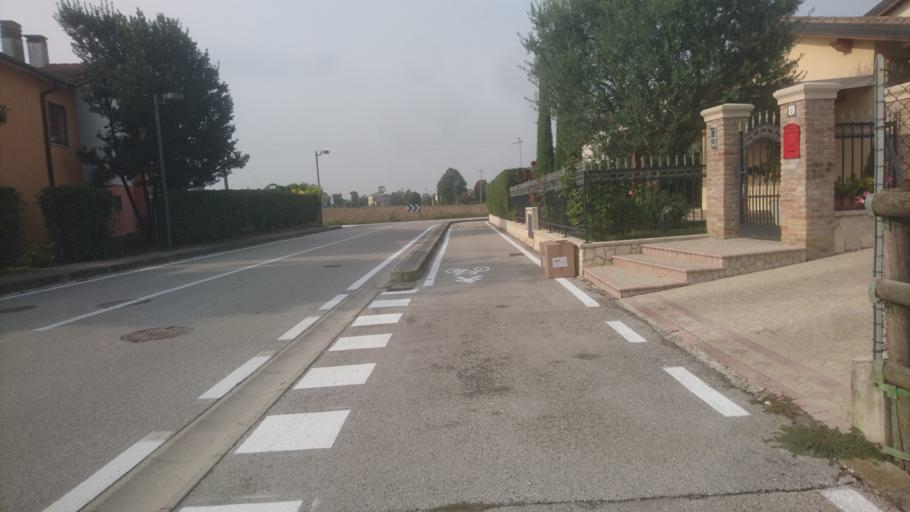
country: IT
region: Veneto
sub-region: Provincia di Vicenza
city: Montegalda
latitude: 45.4525
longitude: 11.6621
